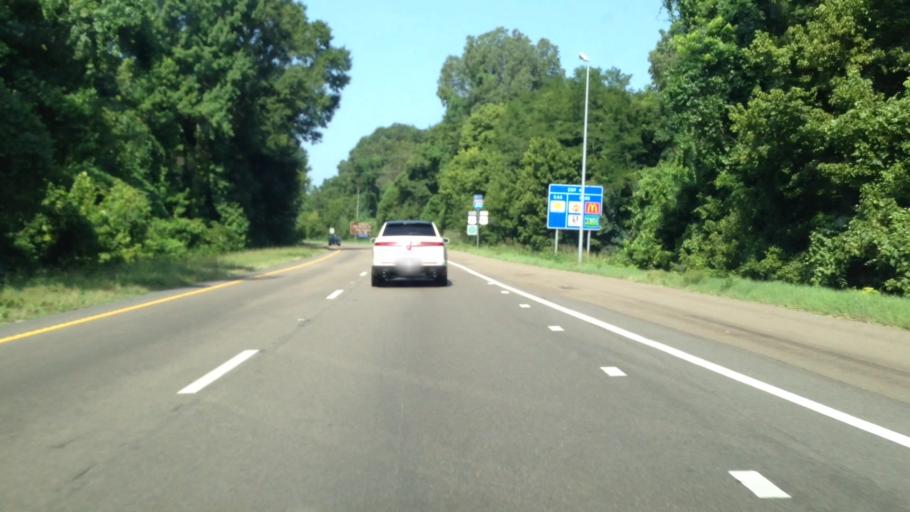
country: US
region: Mississippi
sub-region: Warren County
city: Beechwood
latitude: 32.3479
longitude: -90.8346
